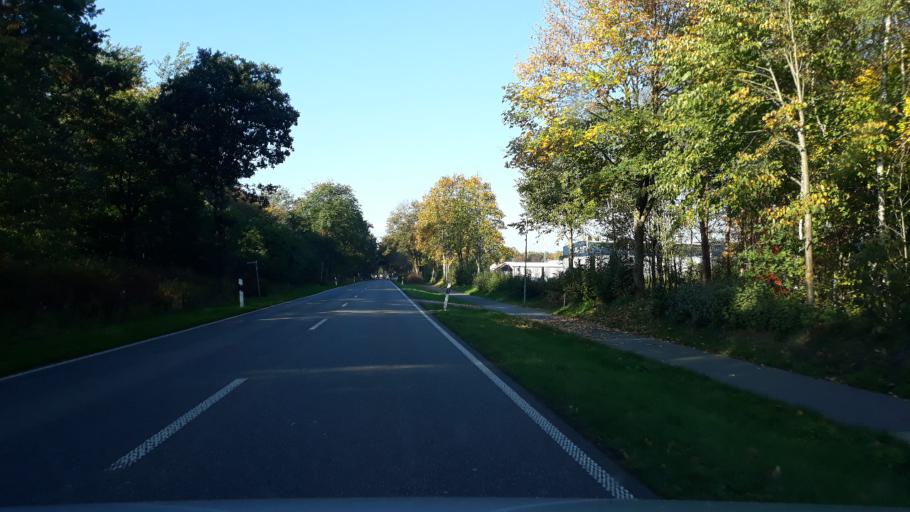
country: DE
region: Schleswig-Holstein
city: Kropp
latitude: 54.4122
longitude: 9.5274
